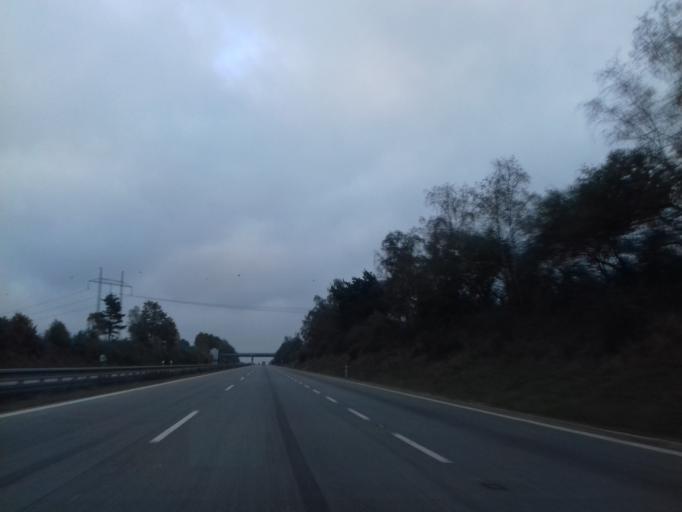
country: CZ
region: Central Bohemia
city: Cechtice
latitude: 49.6522
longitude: 15.1230
